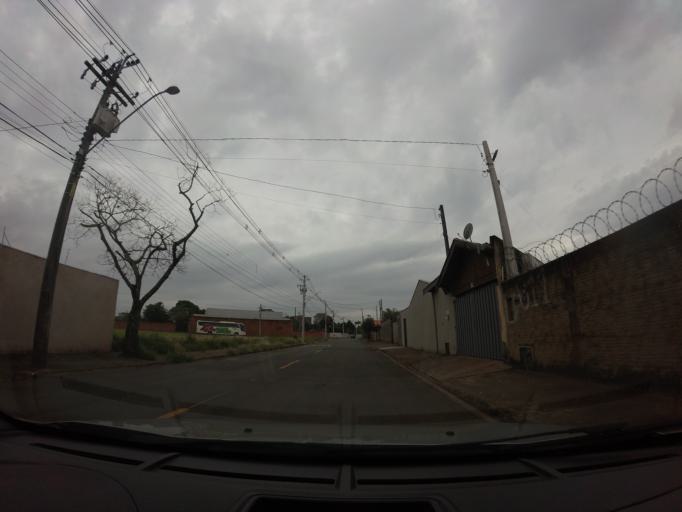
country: BR
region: Sao Paulo
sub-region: Piracicaba
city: Piracicaba
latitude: -22.7459
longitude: -47.5930
